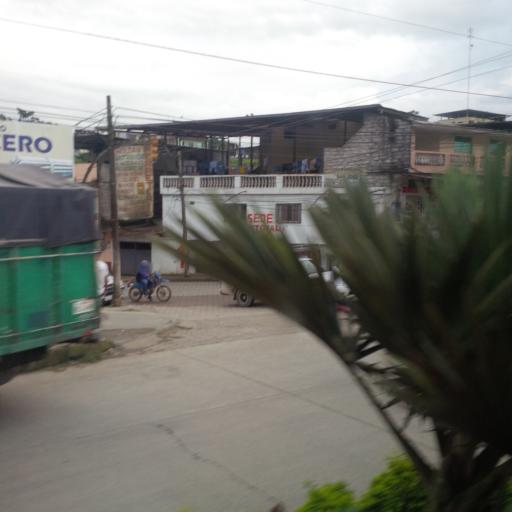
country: EC
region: Chimborazo
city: Alausi
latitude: -2.2047
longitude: -79.1326
